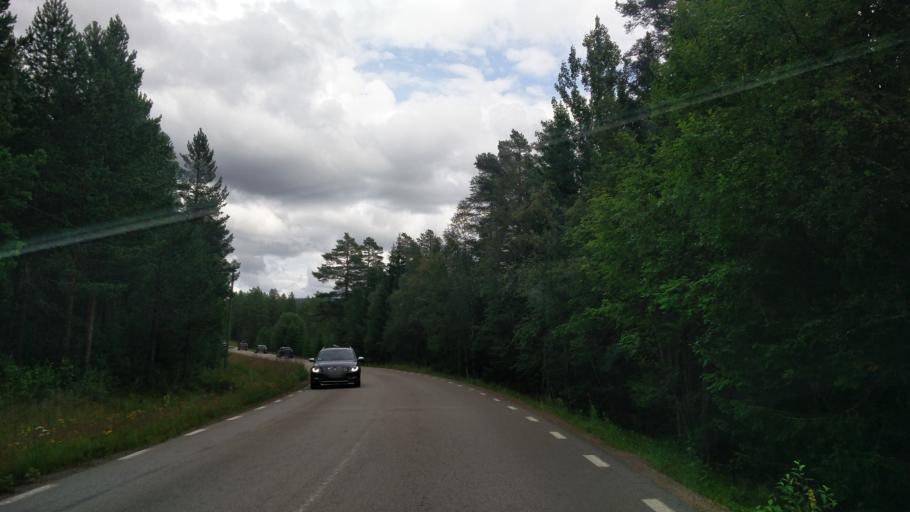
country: NO
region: Hedmark
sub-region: Trysil
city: Innbygda
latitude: 61.1755
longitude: 12.8671
